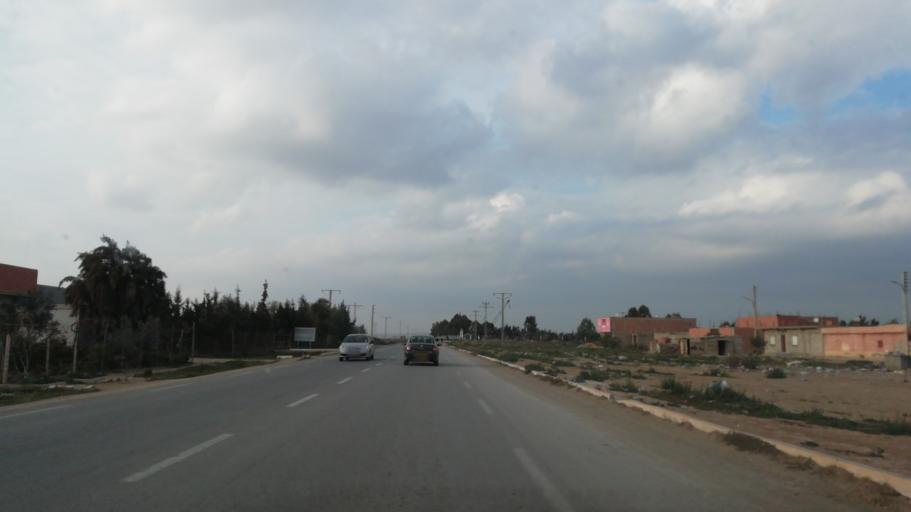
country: DZ
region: Mascara
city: Sig
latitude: 35.6920
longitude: -0.0189
